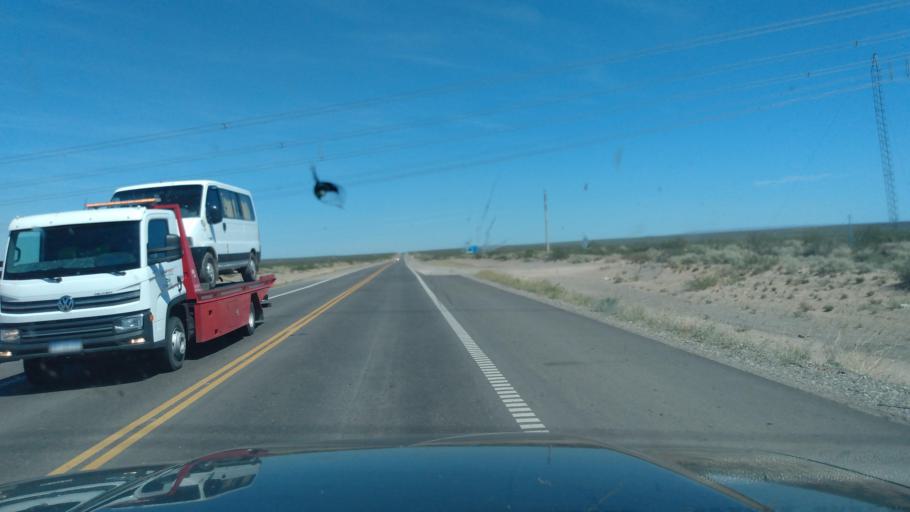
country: AR
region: Neuquen
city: Senillosa
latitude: -39.0742
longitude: -68.5996
